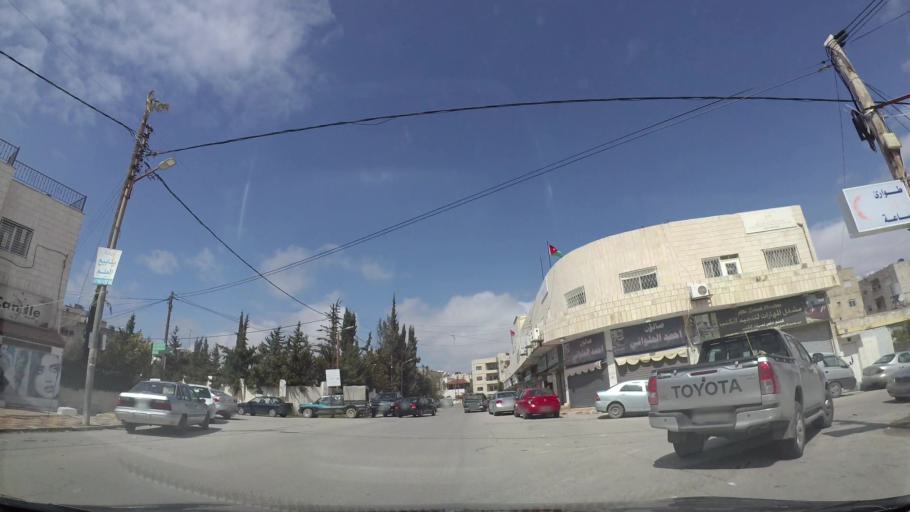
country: JO
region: Amman
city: Wadi as Sir
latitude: 31.9568
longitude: 35.8391
